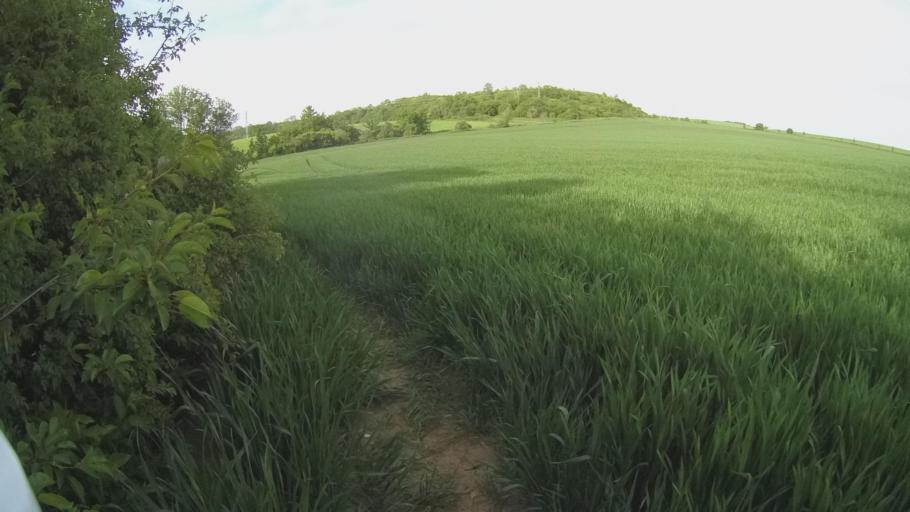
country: CZ
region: Praha
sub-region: Praha 19
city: Kbely
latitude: 50.1664
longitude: 14.5518
